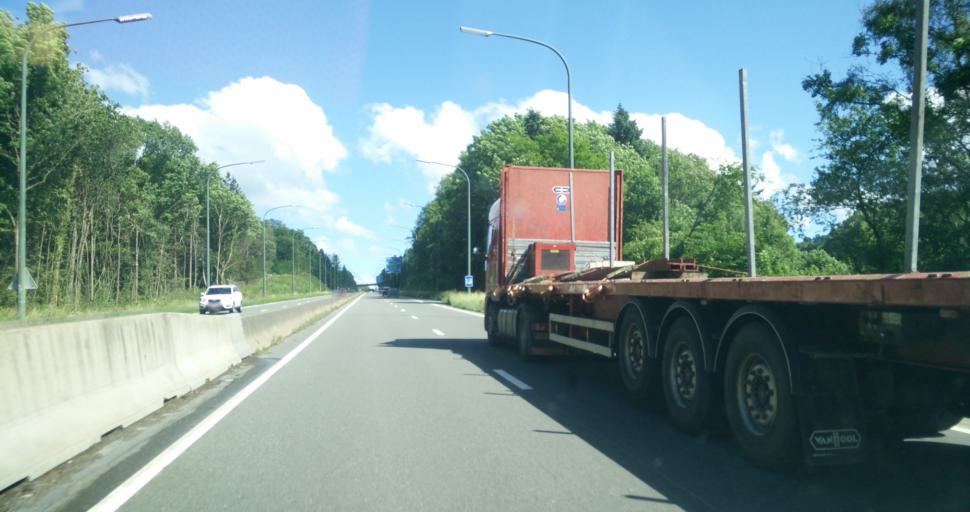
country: BE
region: Wallonia
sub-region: Province du Luxembourg
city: Marche-en-Famenne
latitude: 50.2174
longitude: 5.3471
